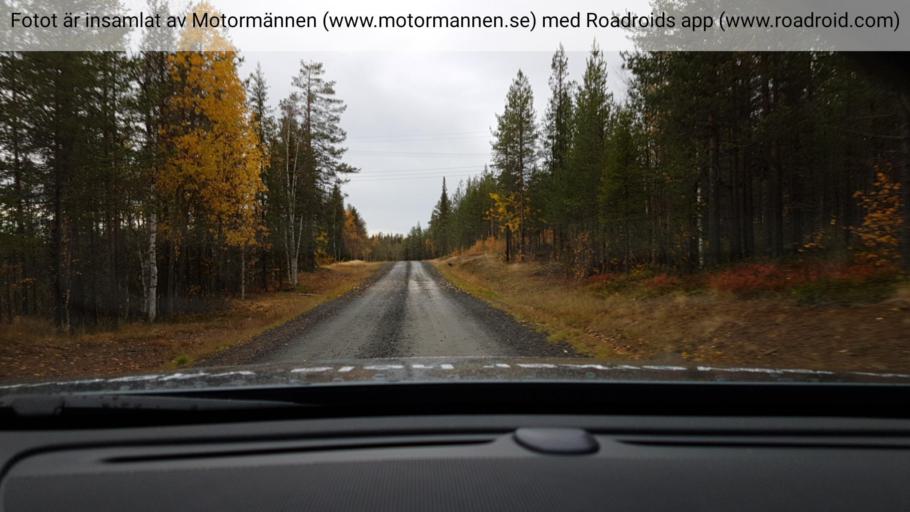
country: SE
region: Norrbotten
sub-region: Pajala Kommun
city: Pajala
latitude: 67.1200
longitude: 22.6888
